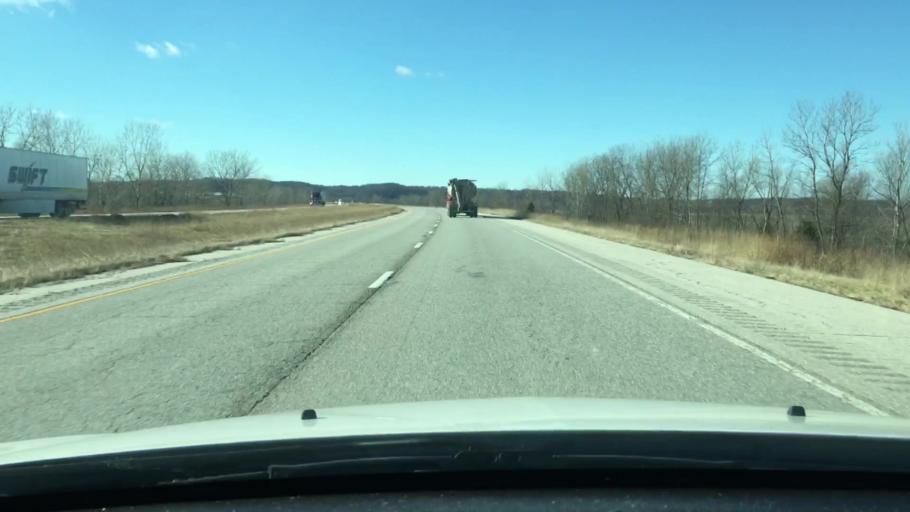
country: US
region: Illinois
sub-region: Pike County
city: Griggsville
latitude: 39.6918
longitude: -90.6099
